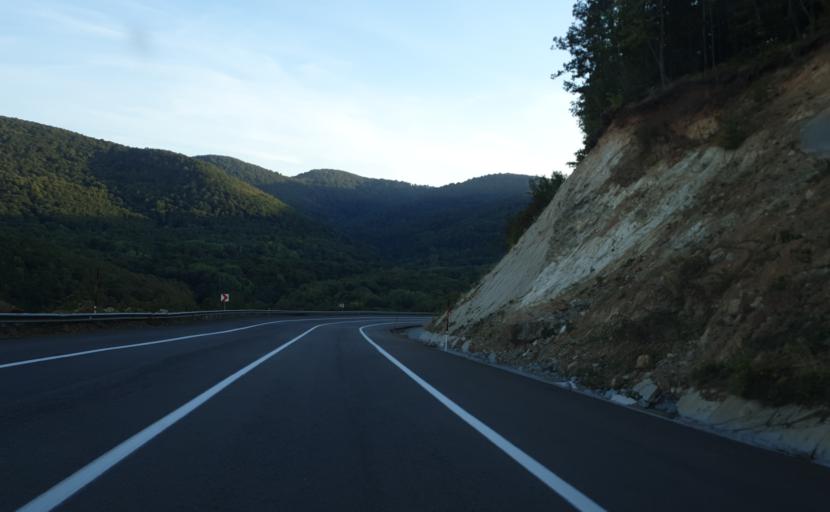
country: TR
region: Kirklareli
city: Sergen
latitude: 41.8122
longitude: 27.7476
